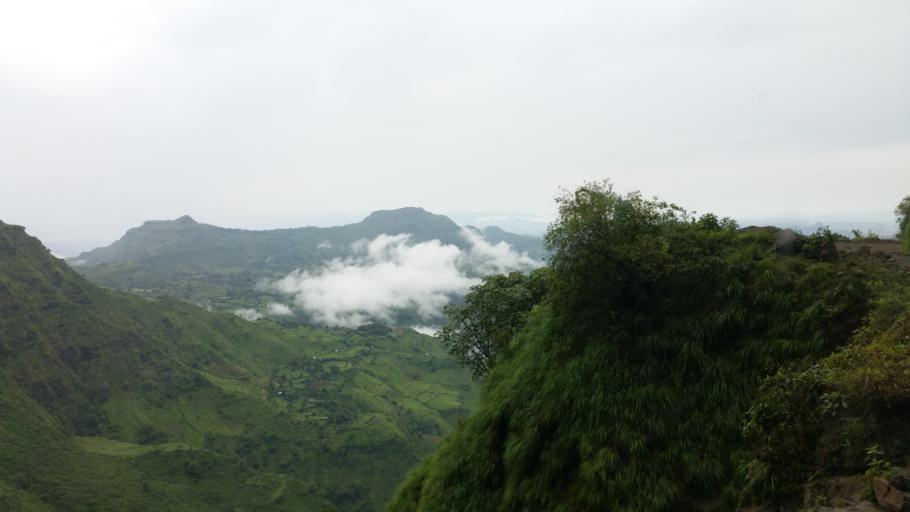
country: ET
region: Amhara
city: Debark'
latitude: 13.1988
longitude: 37.8864
